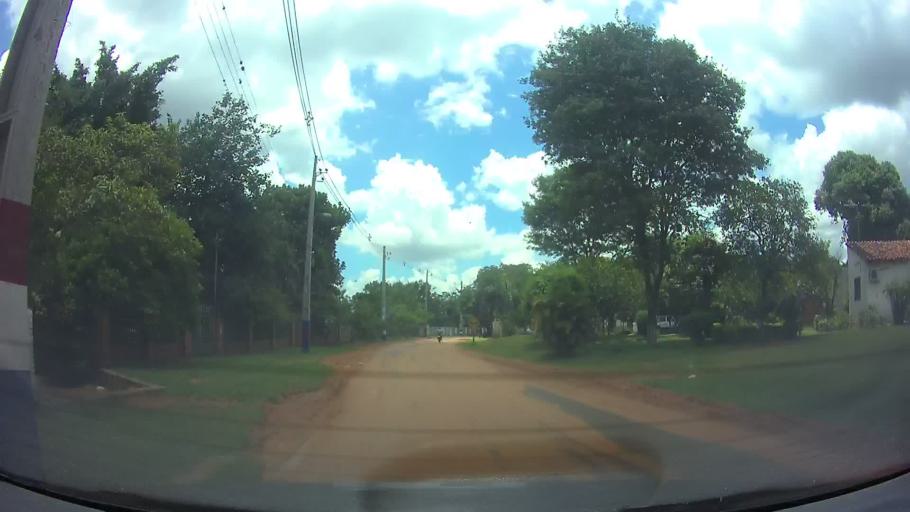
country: PY
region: Central
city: Capiata
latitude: -25.3249
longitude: -57.4262
